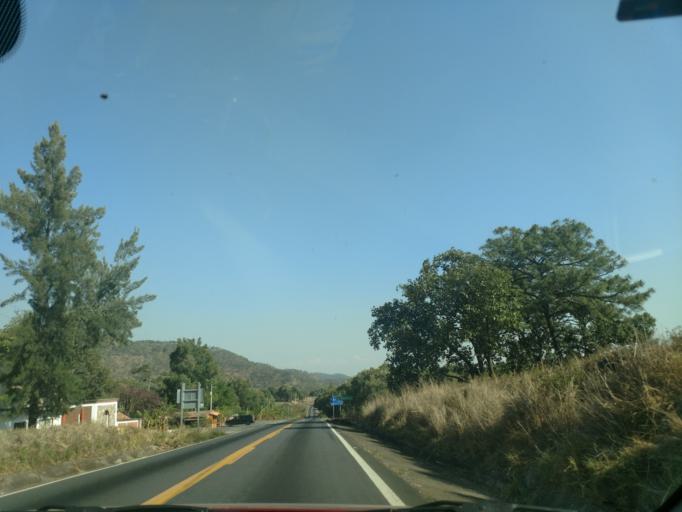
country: MX
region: Nayarit
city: Santa Maria del Oro
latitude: 21.2703
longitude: -104.6474
